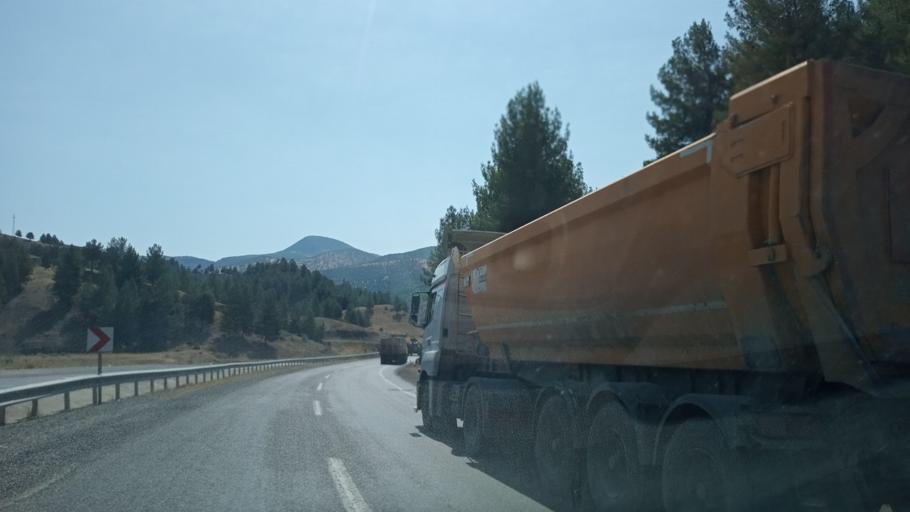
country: TR
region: Siirt
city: Baykan
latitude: 38.1336
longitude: 41.7431
